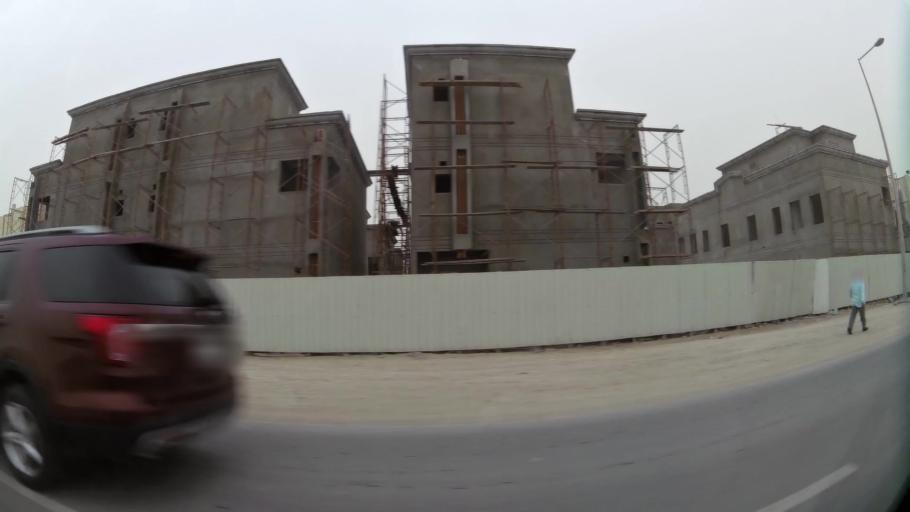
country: QA
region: Baladiyat ad Dawhah
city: Doha
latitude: 25.2406
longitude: 51.4835
